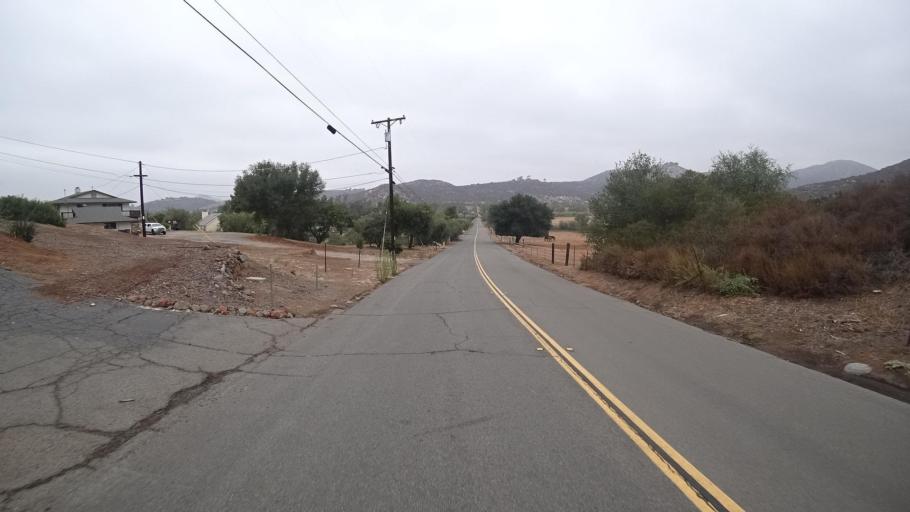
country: US
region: California
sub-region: San Diego County
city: Poway
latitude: 32.9525
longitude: -117.0065
